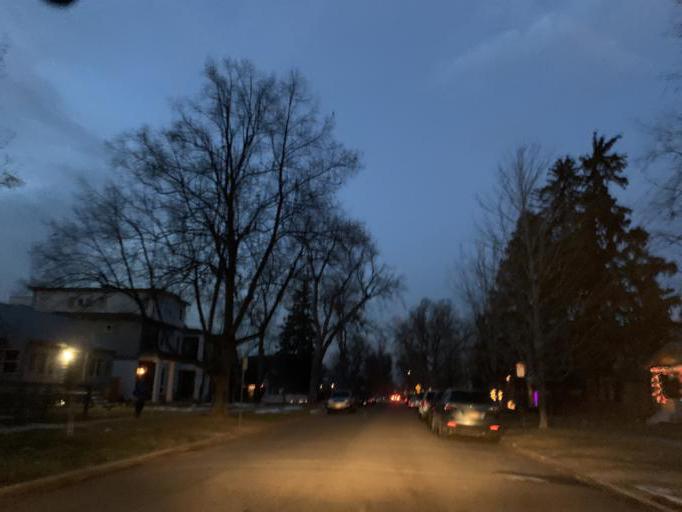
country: US
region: Colorado
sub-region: Jefferson County
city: Edgewater
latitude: 39.7739
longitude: -105.0416
